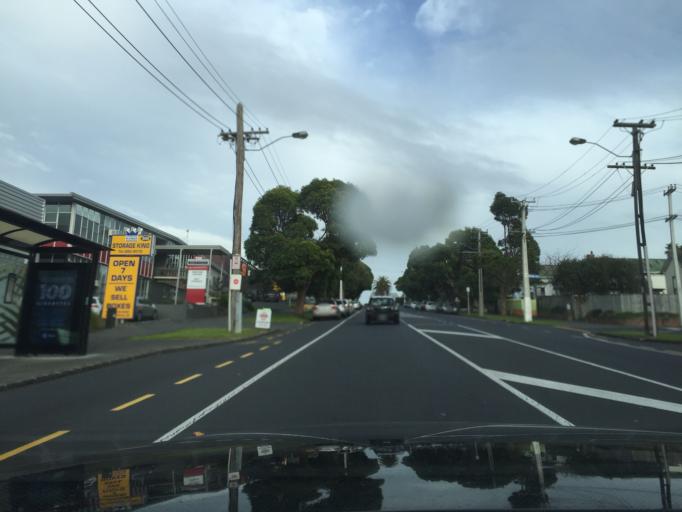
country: NZ
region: Auckland
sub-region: Auckland
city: Auckland
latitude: -36.8546
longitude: 174.7319
